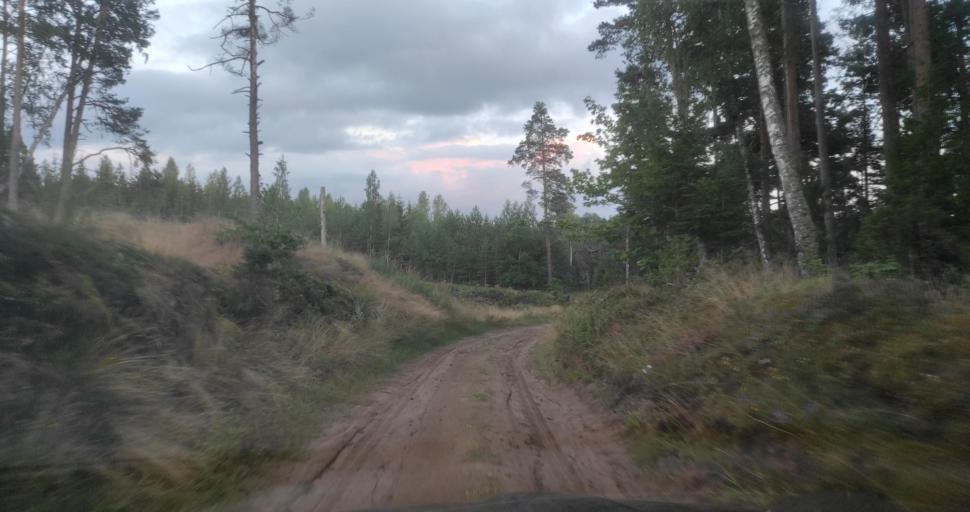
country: LV
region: Kuldigas Rajons
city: Kuldiga
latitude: 57.0648
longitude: 21.8629
